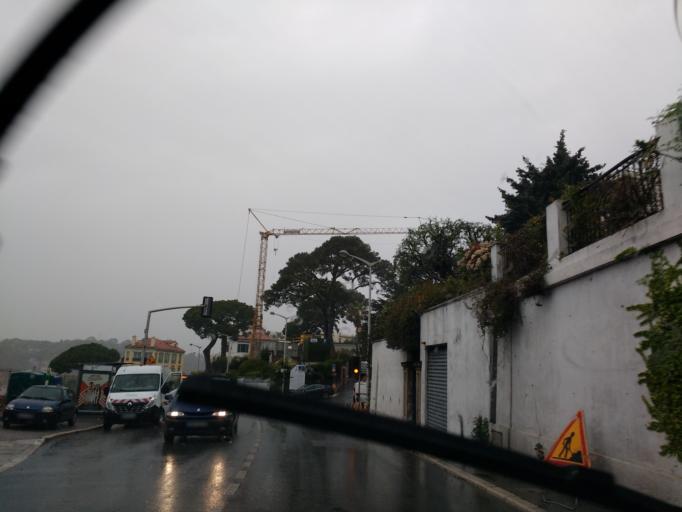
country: FR
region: Provence-Alpes-Cote d'Azur
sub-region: Departement des Alpes-Maritimes
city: Villefranche-sur-Mer
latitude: 43.6917
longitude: 7.2948
